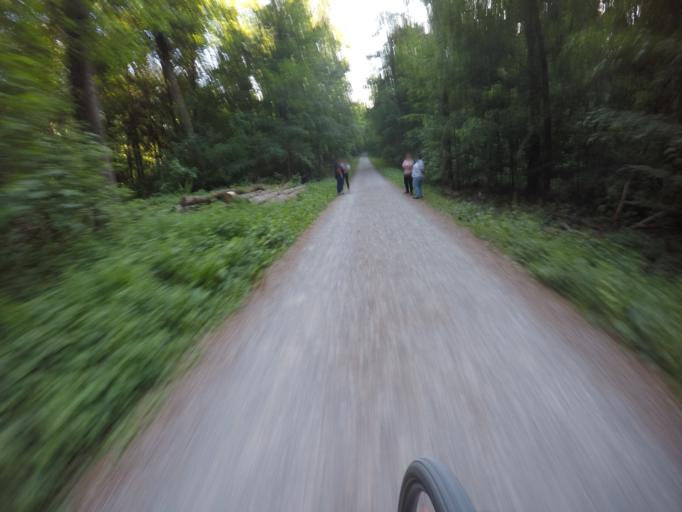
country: DE
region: Baden-Wuerttemberg
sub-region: Regierungsbezirk Stuttgart
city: Fellbach
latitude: 48.7881
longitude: 9.2935
